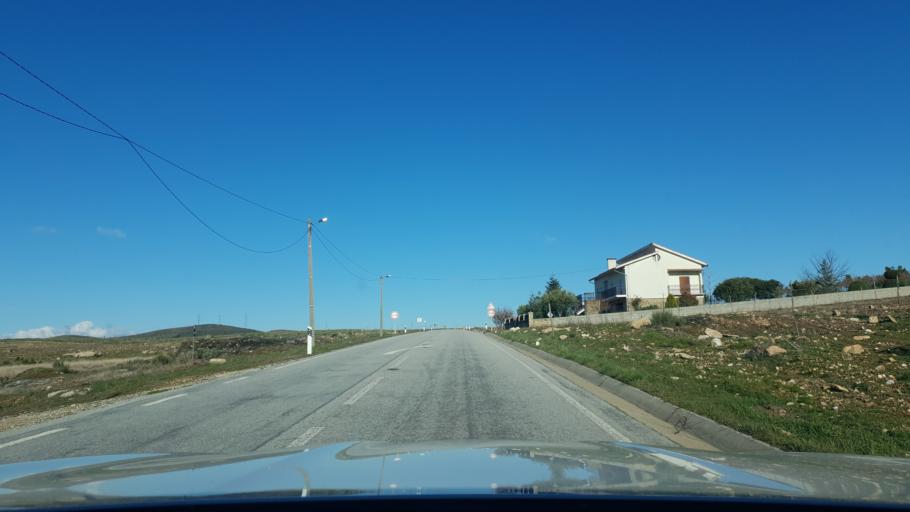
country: PT
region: Braganca
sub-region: Freixo de Espada A Cinta
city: Freixo de Espada a Cinta
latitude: 41.1801
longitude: -6.8083
